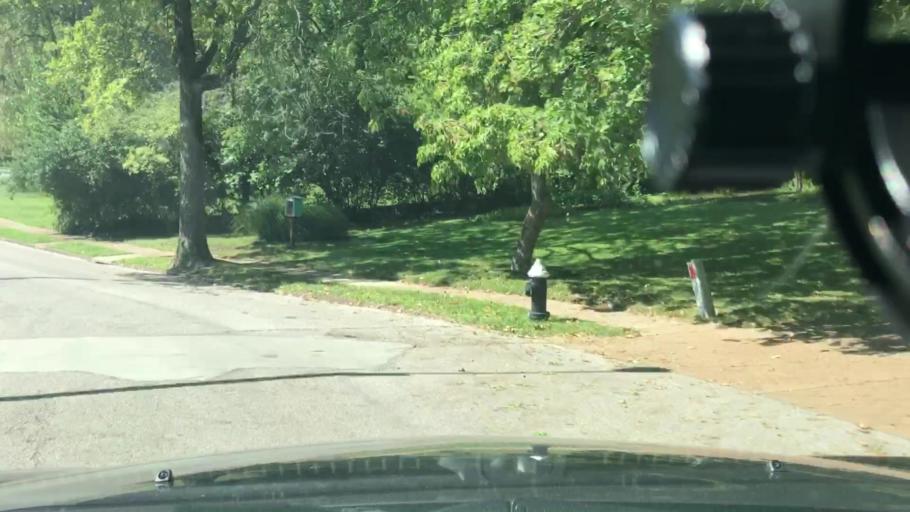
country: US
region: Missouri
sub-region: Saint Louis County
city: Richmond Heights
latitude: 38.6144
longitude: -90.2932
